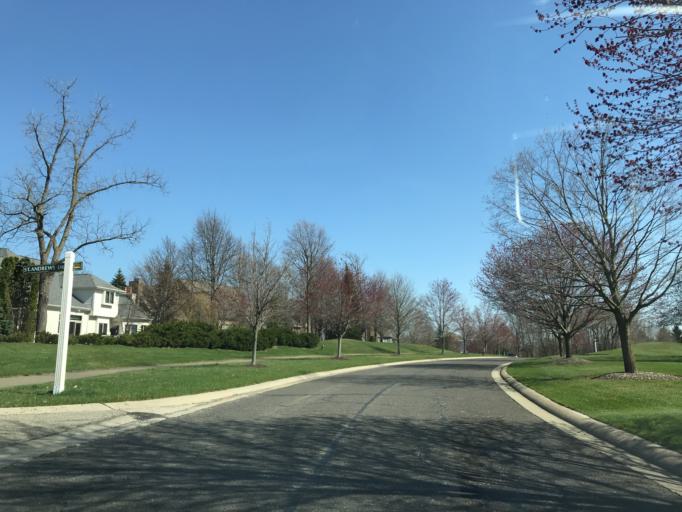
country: US
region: Michigan
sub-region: Oakland County
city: South Lyon
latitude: 42.4576
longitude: -83.5802
